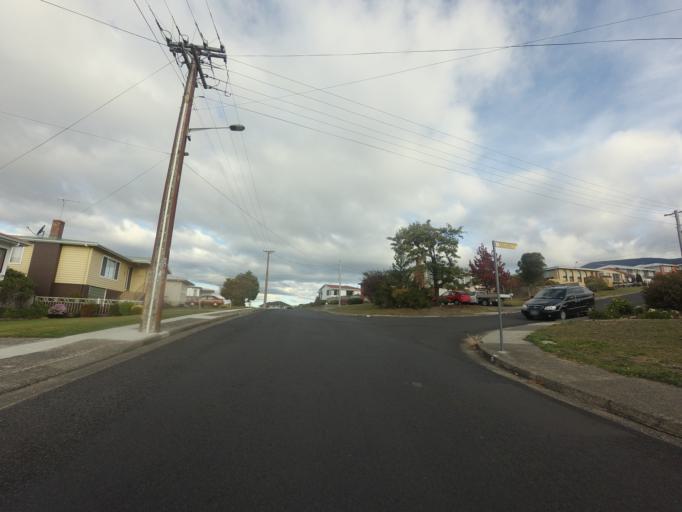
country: AU
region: Tasmania
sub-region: Glenorchy
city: Glenorchy
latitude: -42.8296
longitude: 147.2610
